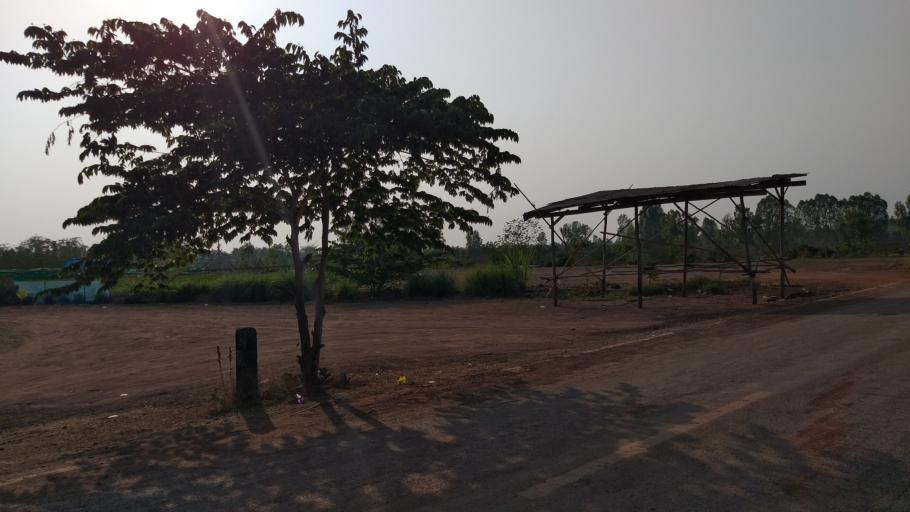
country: TH
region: Changwat Udon Thani
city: Ban Dung
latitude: 17.7426
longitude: 103.3569
